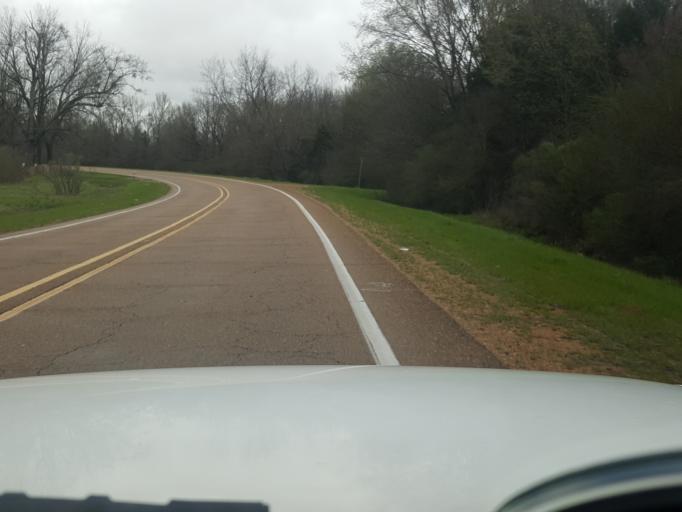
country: US
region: Mississippi
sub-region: Madison County
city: Canton
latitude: 32.7515
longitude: -90.1448
